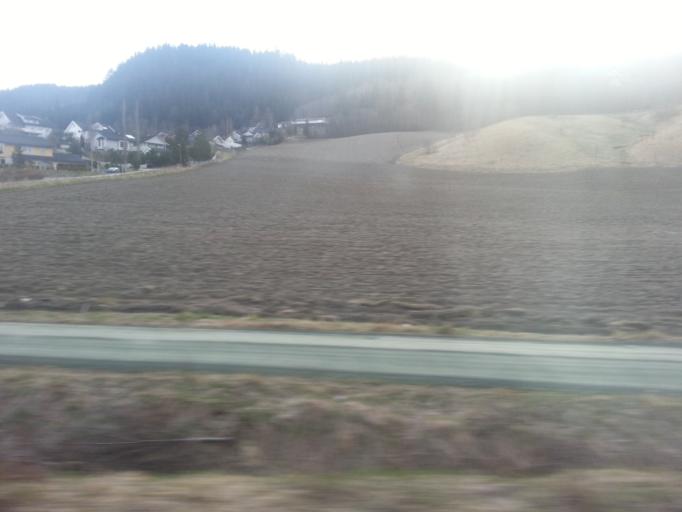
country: NO
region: Sor-Trondelag
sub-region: Melhus
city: Melhus
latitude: 63.2311
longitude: 10.2828
